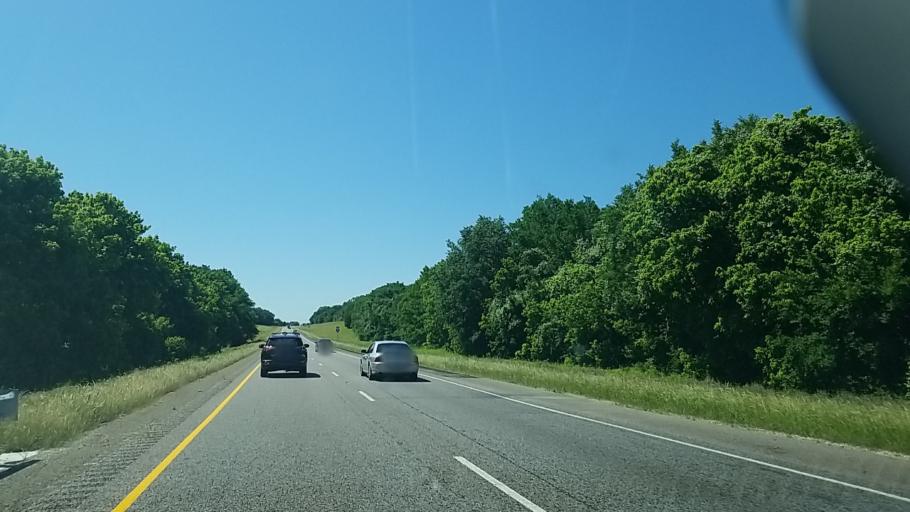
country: US
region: Texas
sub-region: Freestone County
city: Fairfield
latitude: 31.8102
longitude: -96.2685
